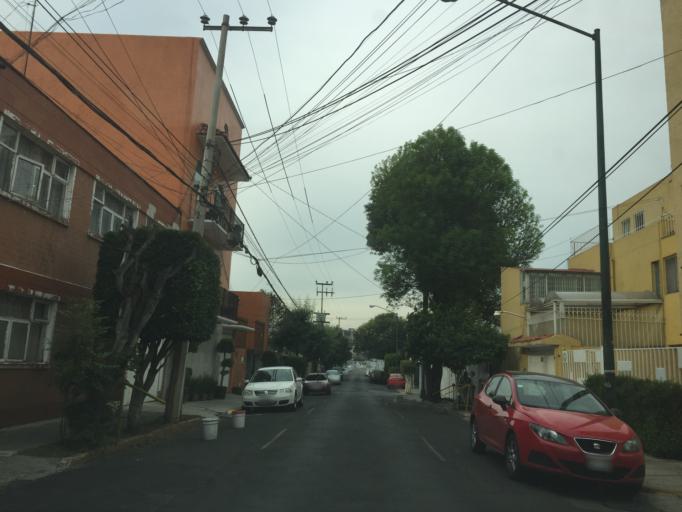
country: MX
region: Mexico
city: Colonia Lindavista
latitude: 19.4964
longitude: -99.1313
